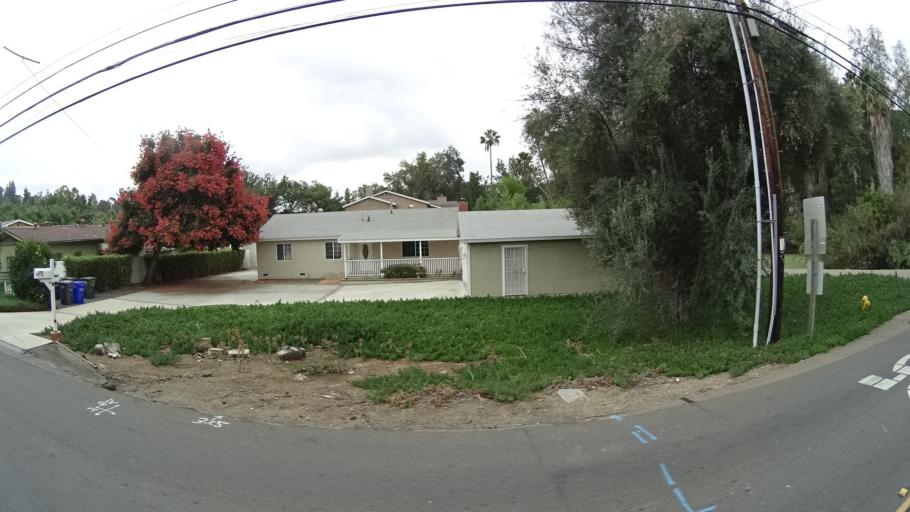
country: US
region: California
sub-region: San Diego County
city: Spring Valley
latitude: 32.7580
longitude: -117.0003
